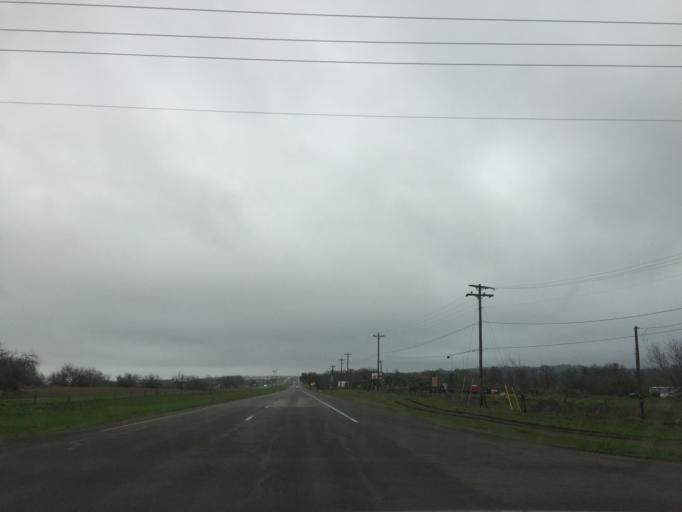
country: US
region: Texas
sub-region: Travis County
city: Garfield
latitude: 30.1829
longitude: -97.5418
